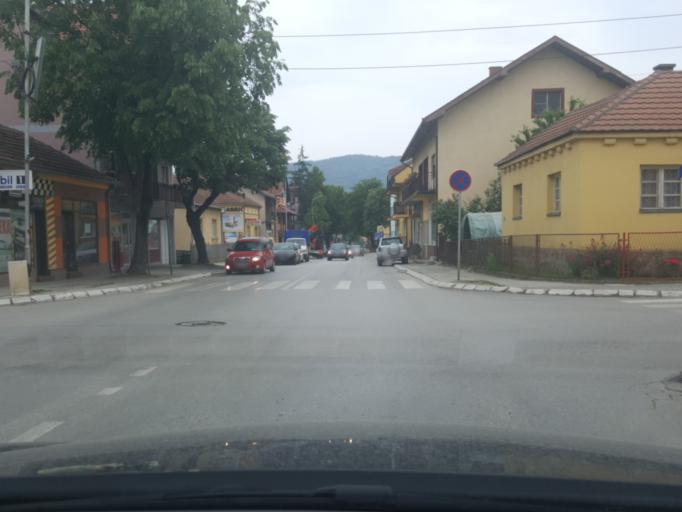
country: RS
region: Central Serbia
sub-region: Zlatiborski Okrug
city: Bajina Basta
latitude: 43.9697
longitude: 19.5646
